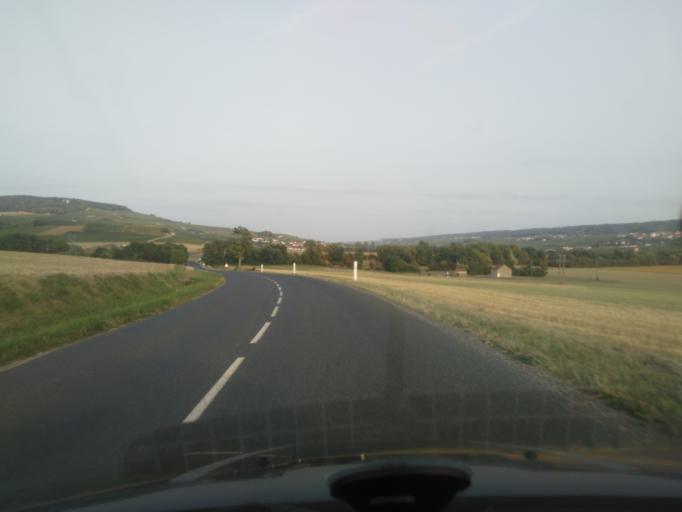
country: FR
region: Champagne-Ardenne
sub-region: Departement de la Marne
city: Mareuil-le-Port
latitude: 49.0885
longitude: 3.7732
